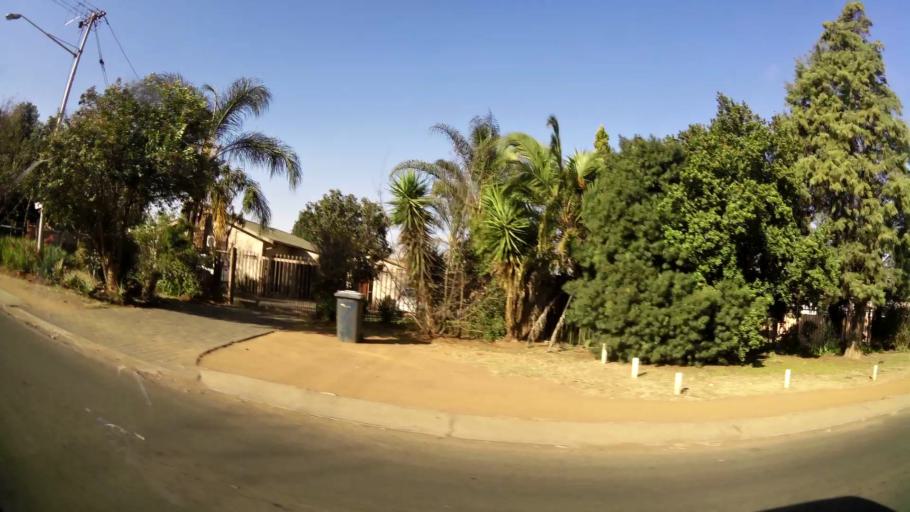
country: ZA
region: Gauteng
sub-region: City of Tshwane Metropolitan Municipality
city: Pretoria
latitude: -25.7098
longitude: 28.2609
